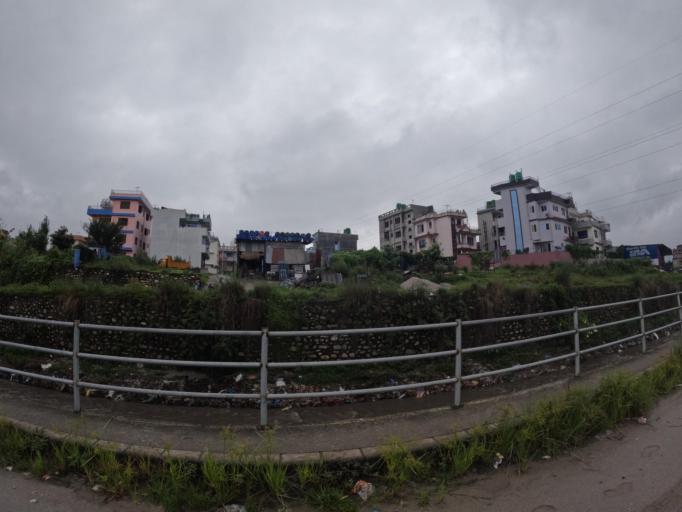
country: NP
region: Central Region
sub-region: Bagmati Zone
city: Kathmandu
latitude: 27.7628
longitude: 85.3177
